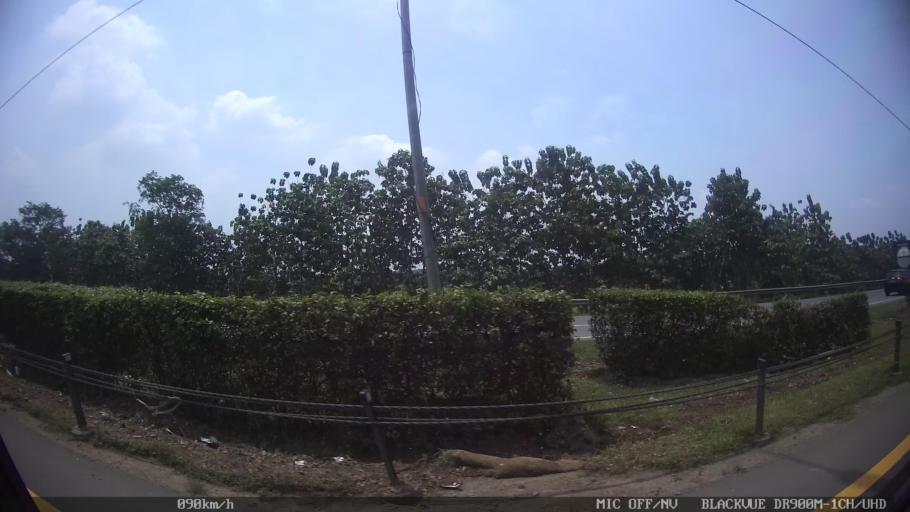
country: ID
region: West Java
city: Kresek
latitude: -6.1525
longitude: 106.3154
